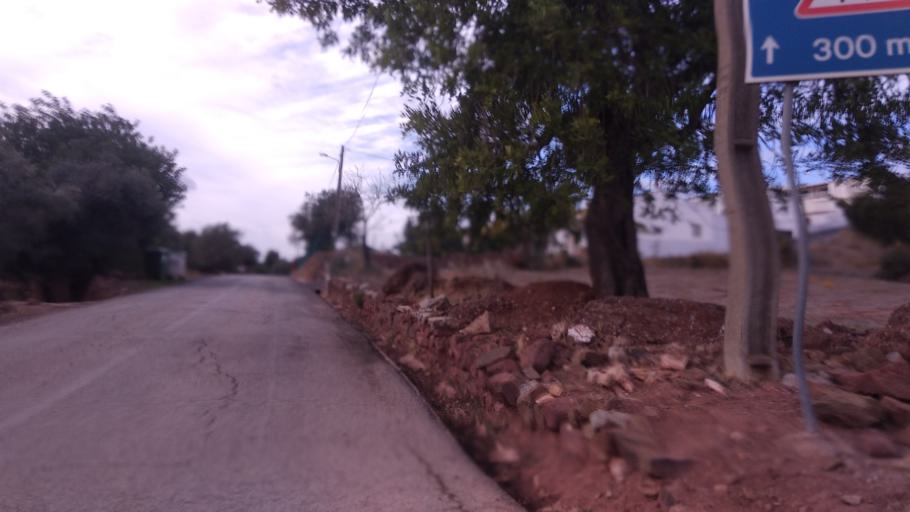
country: PT
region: Faro
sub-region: Sao Bras de Alportel
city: Sao Bras de Alportel
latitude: 37.1752
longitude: -7.9012
